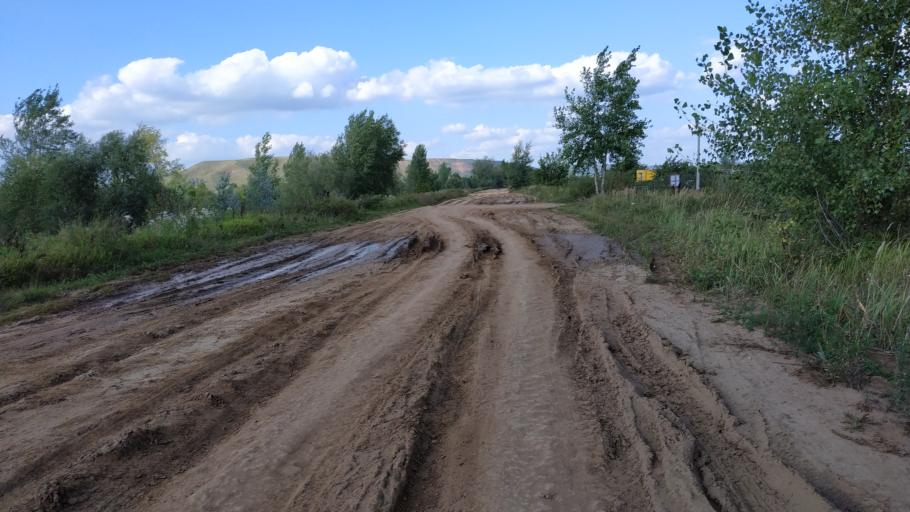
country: RU
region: Tatarstan
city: Nizhnekamsk
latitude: 55.6842
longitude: 51.7314
